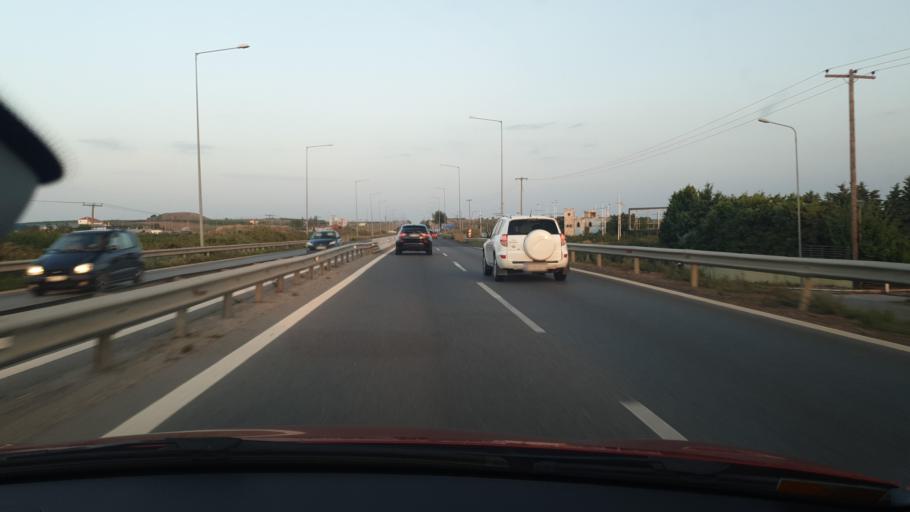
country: GR
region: Central Macedonia
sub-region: Nomos Chalkidikis
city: Nea Plagia
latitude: 40.2770
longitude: 23.2045
